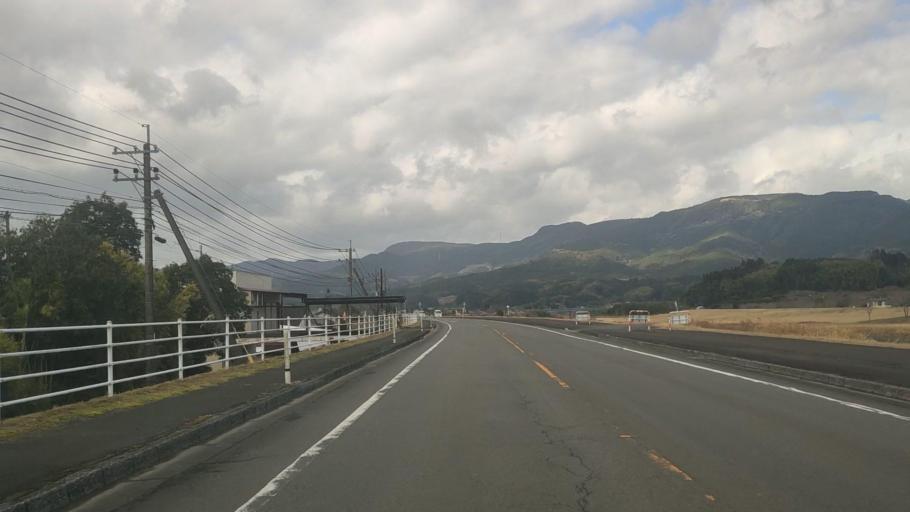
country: JP
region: Kumamoto
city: Hitoyoshi
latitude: 32.0545
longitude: 130.7983
